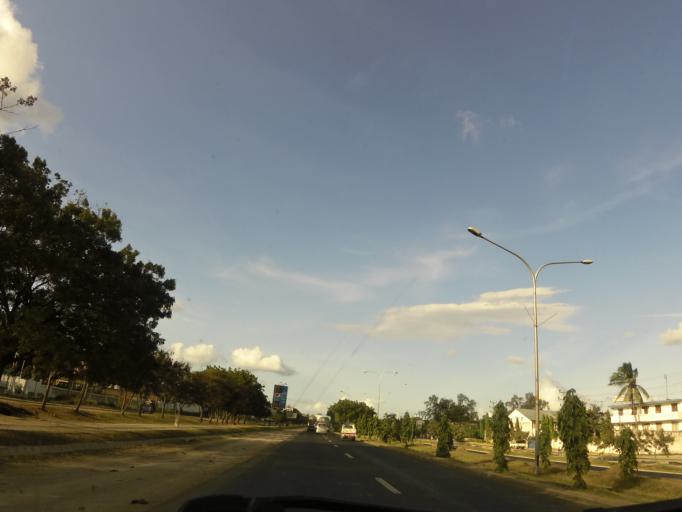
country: TZ
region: Dar es Salaam
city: Dar es Salaam
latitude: -6.8498
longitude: 39.2336
